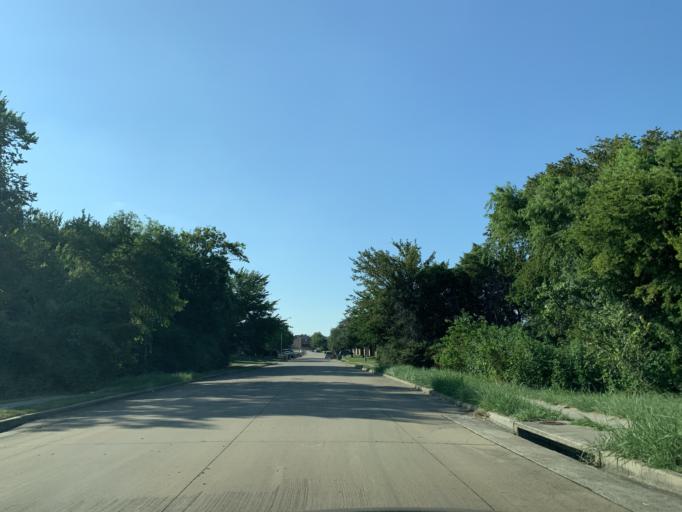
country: US
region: Texas
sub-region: Dallas County
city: Hutchins
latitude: 32.6552
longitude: -96.7651
